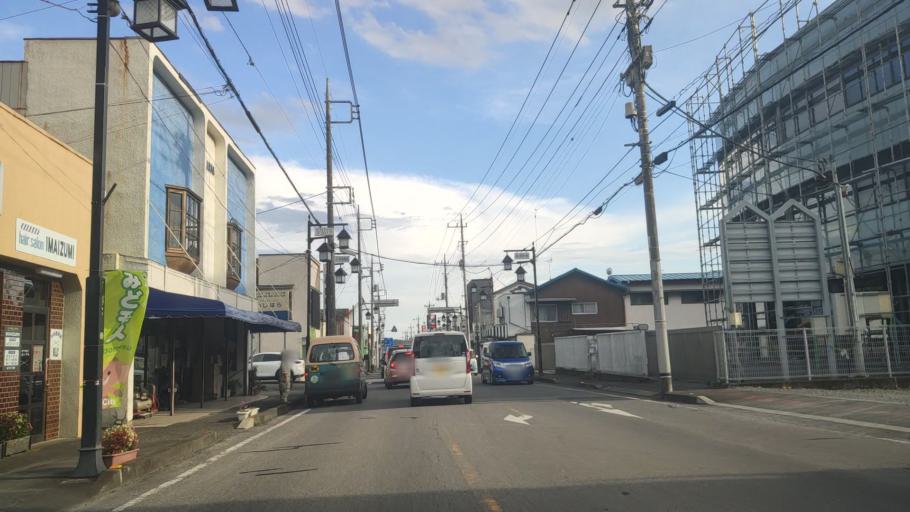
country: JP
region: Gunma
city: Omamacho-omama
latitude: 36.4326
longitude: 139.2749
